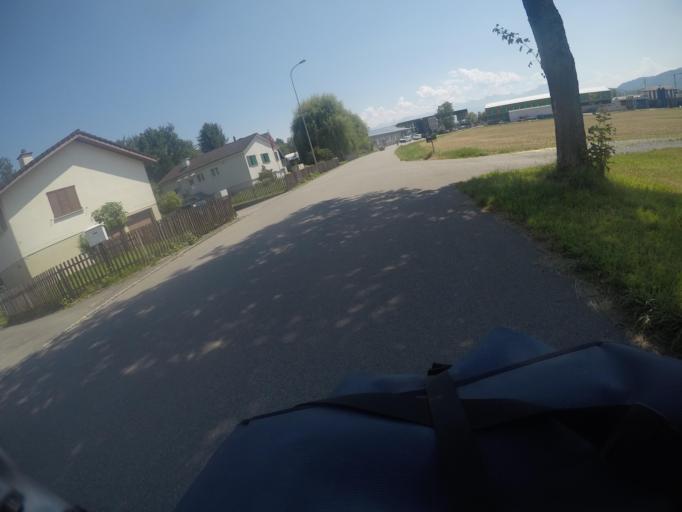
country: CH
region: Saint Gallen
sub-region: Wahlkreis Rheintal
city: Altstatten
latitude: 47.3701
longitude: 9.5581
